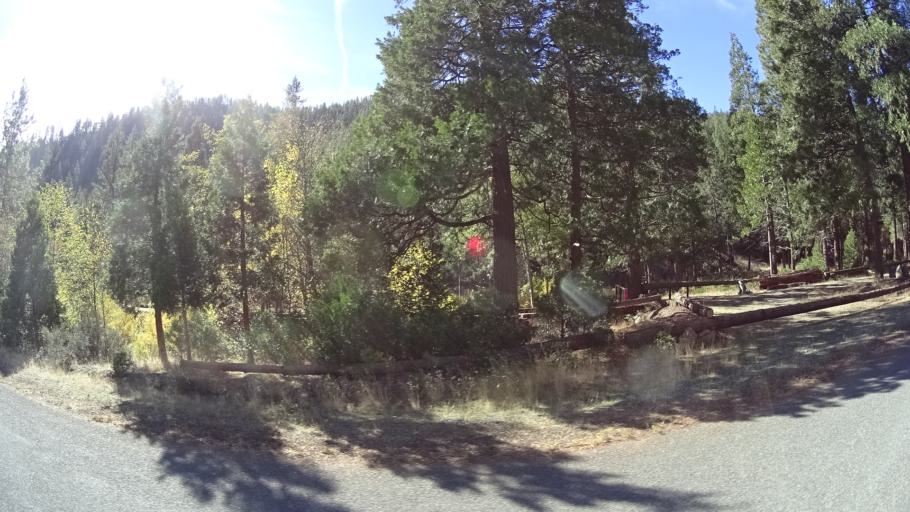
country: US
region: California
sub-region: Siskiyou County
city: Yreka
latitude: 41.6314
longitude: -122.7227
